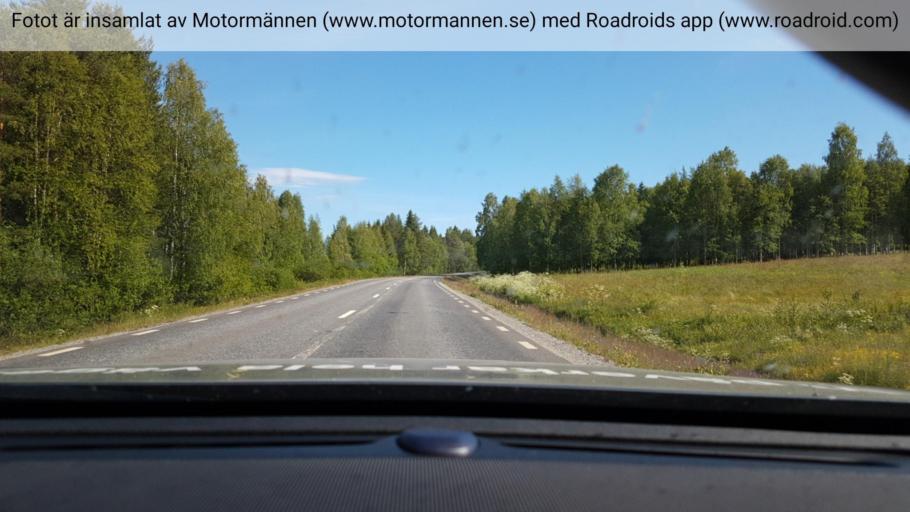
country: SE
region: Vaesterbotten
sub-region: Lycksele Kommun
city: Soderfors
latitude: 64.8173
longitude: 18.0695
